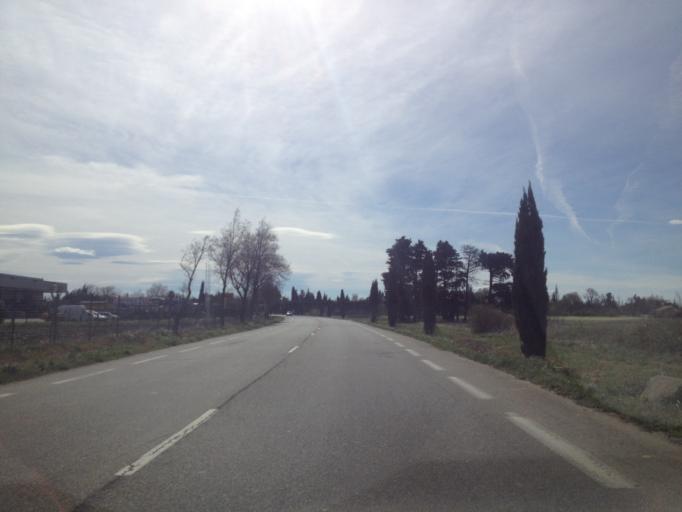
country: FR
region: Provence-Alpes-Cote d'Azur
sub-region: Departement du Vaucluse
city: Camaret-sur-Aigues
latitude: 44.1619
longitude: 4.8593
